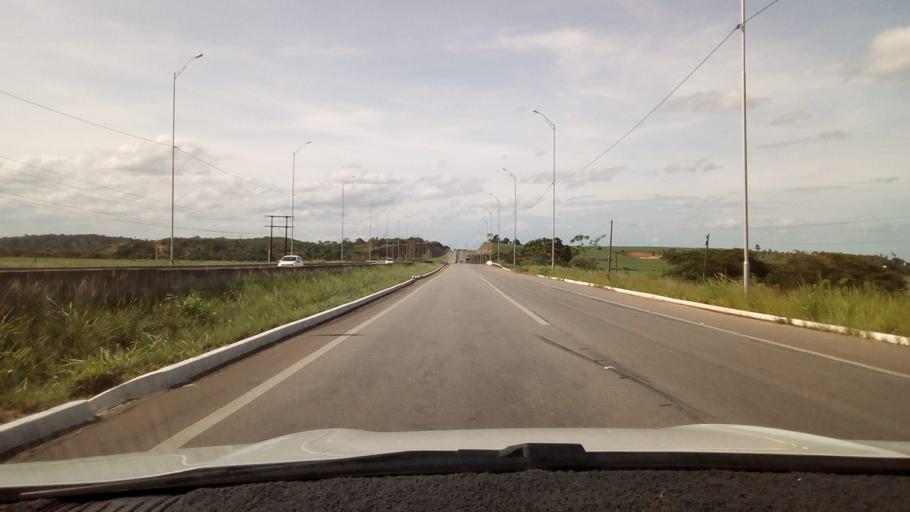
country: BR
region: Paraiba
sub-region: Santa Rita
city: Santa Rita
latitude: -7.1032
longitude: -34.9646
